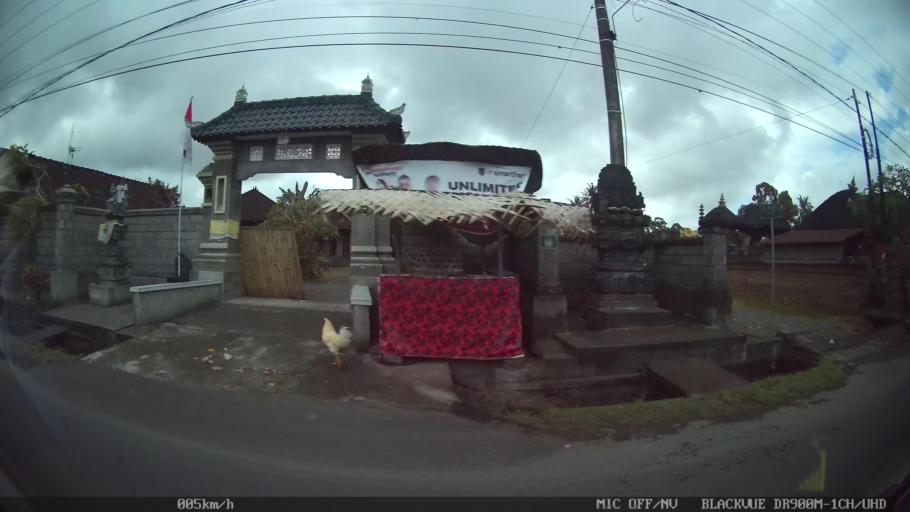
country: ID
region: Bali
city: Banjar Mambalkajanan
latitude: -8.5515
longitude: 115.2117
